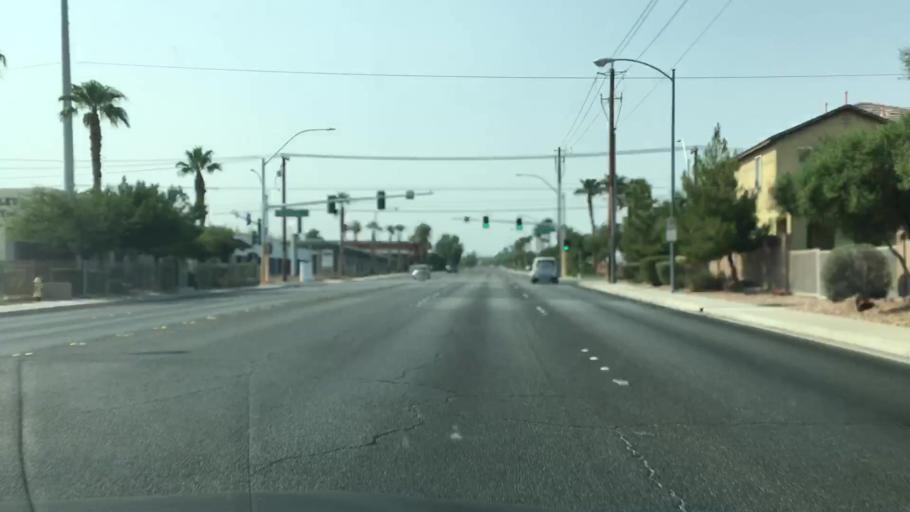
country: US
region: Nevada
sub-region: Clark County
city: Whitney
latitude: 36.0793
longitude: -115.0915
